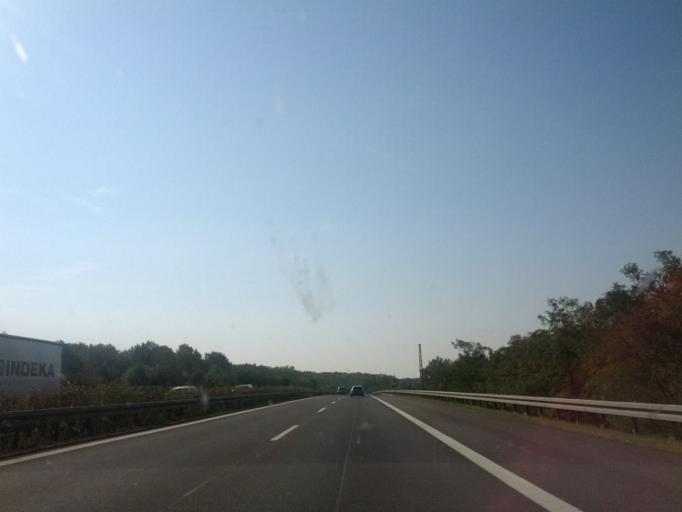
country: DE
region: Brandenburg
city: Bernau bei Berlin
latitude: 52.6706
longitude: 13.5675
